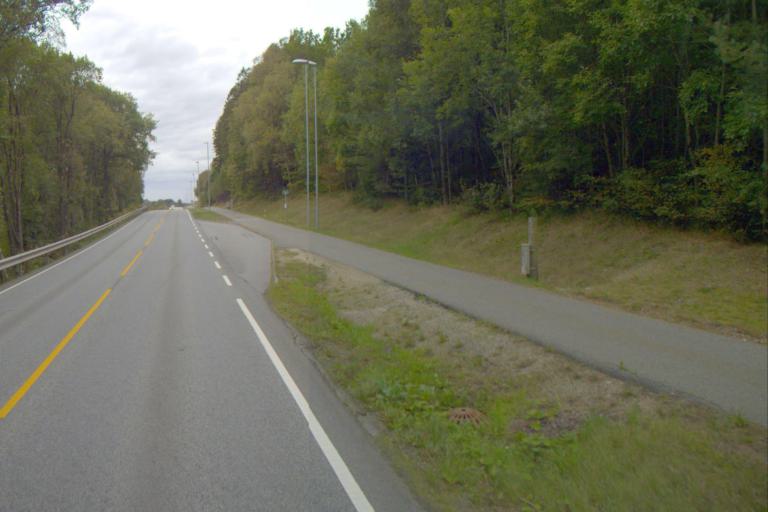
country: NO
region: Rogaland
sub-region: Sandnes
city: Hommersak
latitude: 58.8782
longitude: 5.8281
